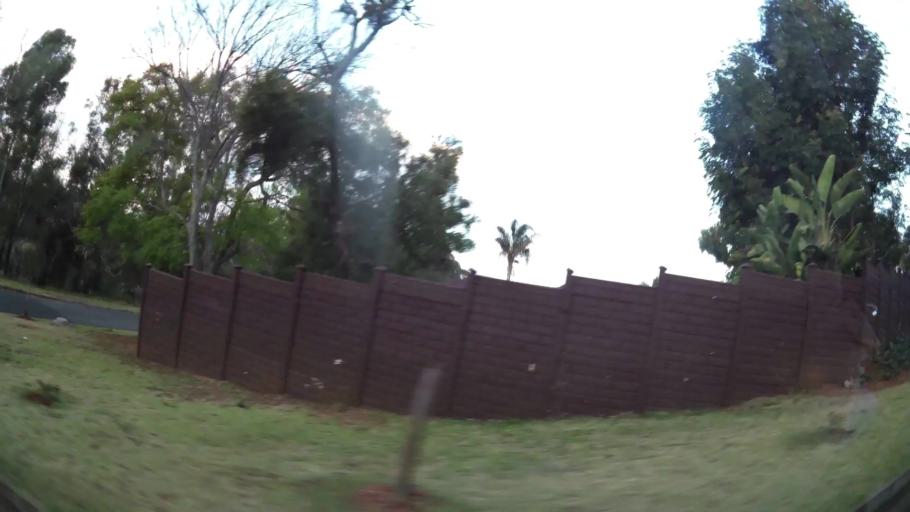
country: ZA
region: Gauteng
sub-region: West Rand District Municipality
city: Krugersdorp
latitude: -26.0744
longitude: 27.7775
